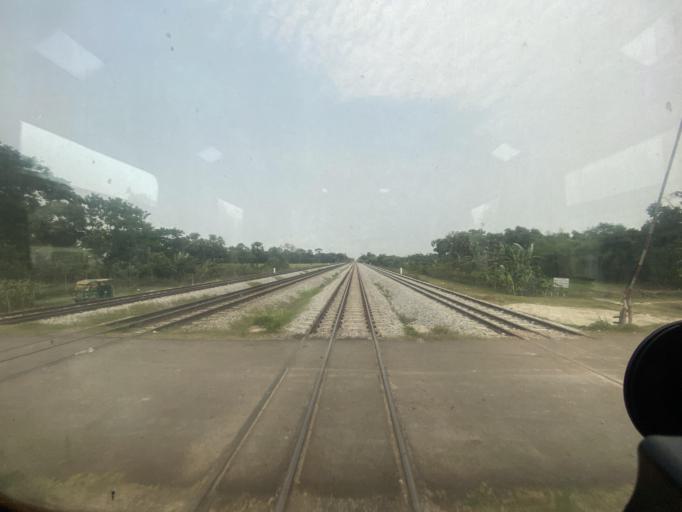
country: BD
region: Chittagong
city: Laksham
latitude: 23.3077
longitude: 91.1388
